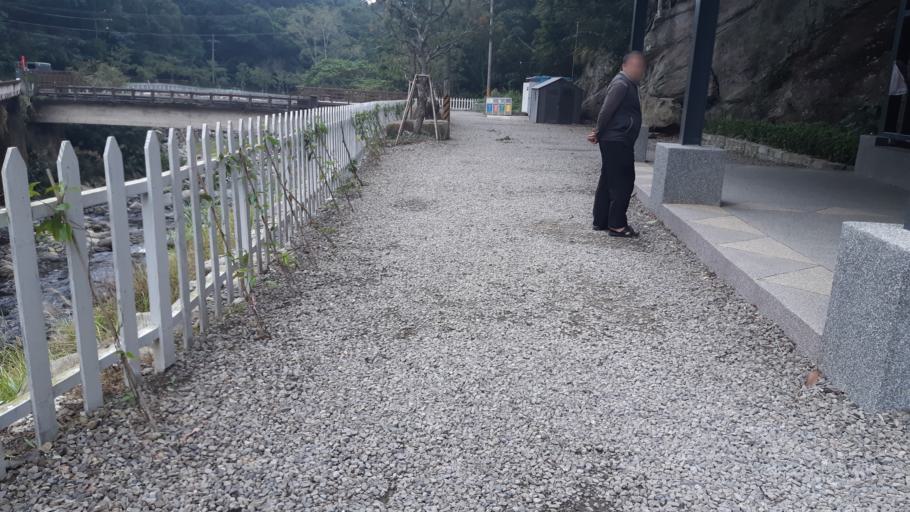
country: TW
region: Taiwan
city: Daxi
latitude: 24.6852
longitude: 121.2304
